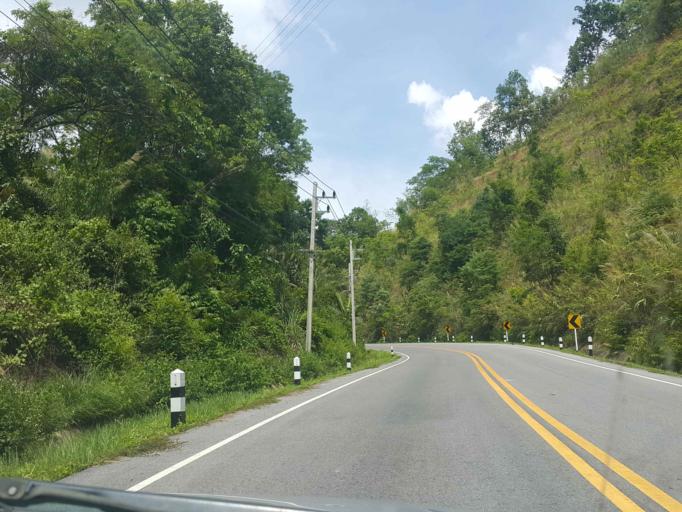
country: TH
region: Nan
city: Ban Luang
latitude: 18.8717
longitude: 100.4807
